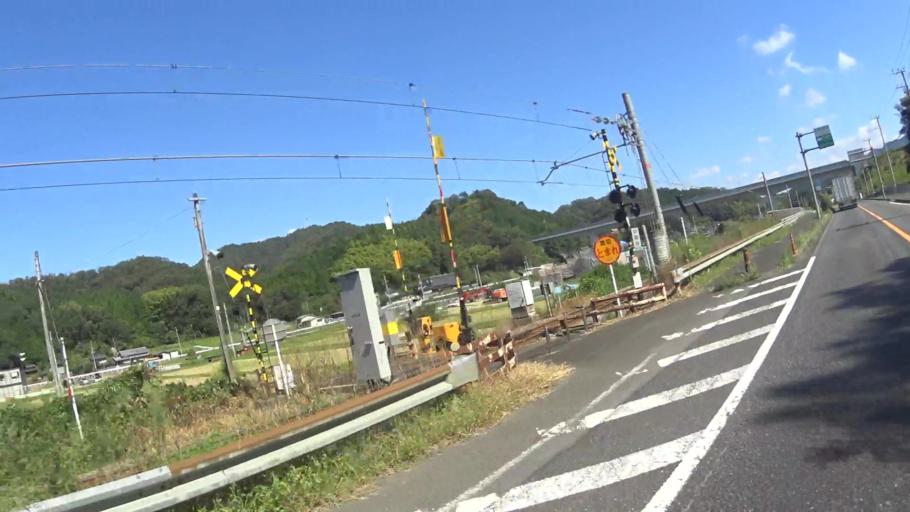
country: JP
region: Kyoto
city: Ayabe
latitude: 35.3360
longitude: 135.3050
